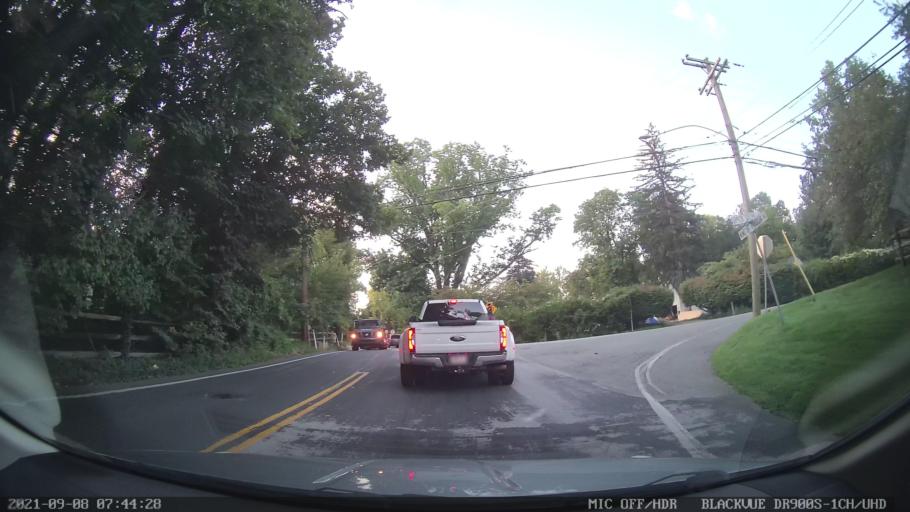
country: US
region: Pennsylvania
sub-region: Delaware County
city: Radnor
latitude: 40.0607
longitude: -75.3734
